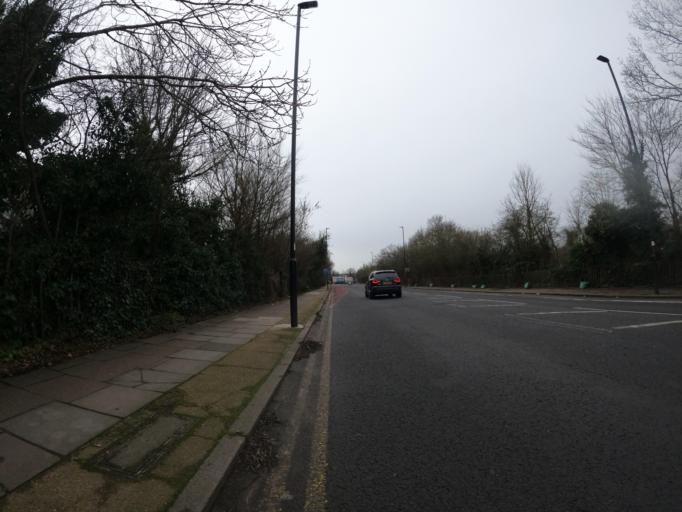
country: GB
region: England
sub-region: Greater London
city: Greenford
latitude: 51.5123
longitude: -0.3549
